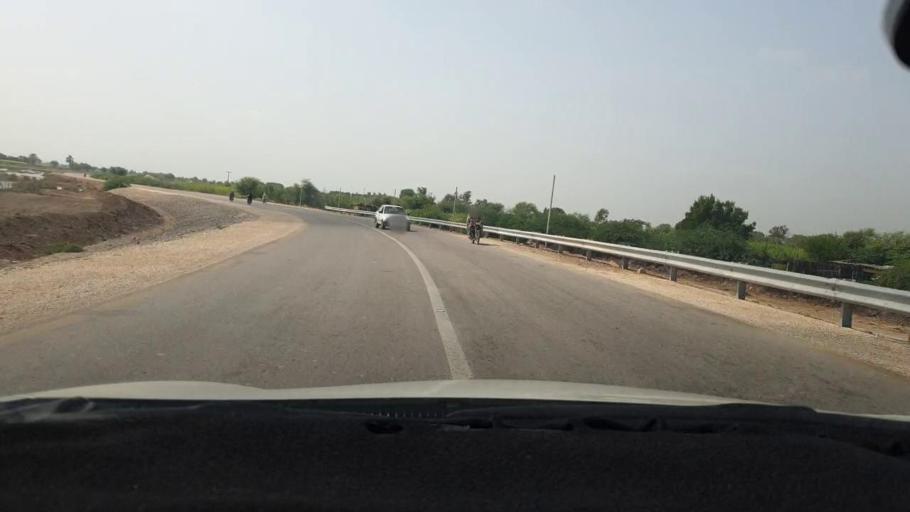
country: PK
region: Sindh
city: Mirpur Khas
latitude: 25.5911
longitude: 69.0758
